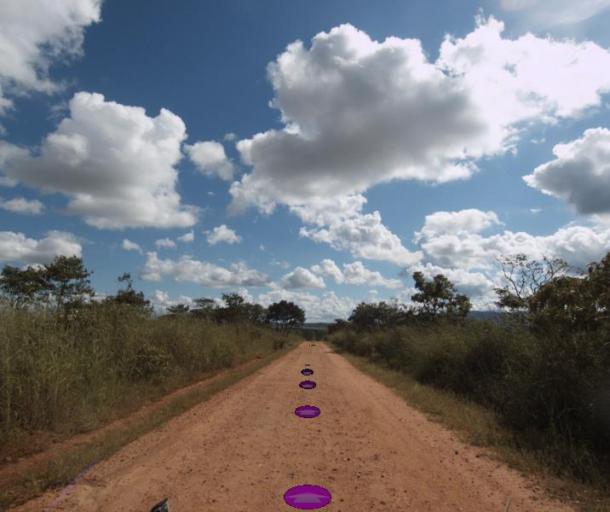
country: BR
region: Goias
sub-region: Jaragua
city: Jaragua
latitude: -15.8206
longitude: -49.2208
